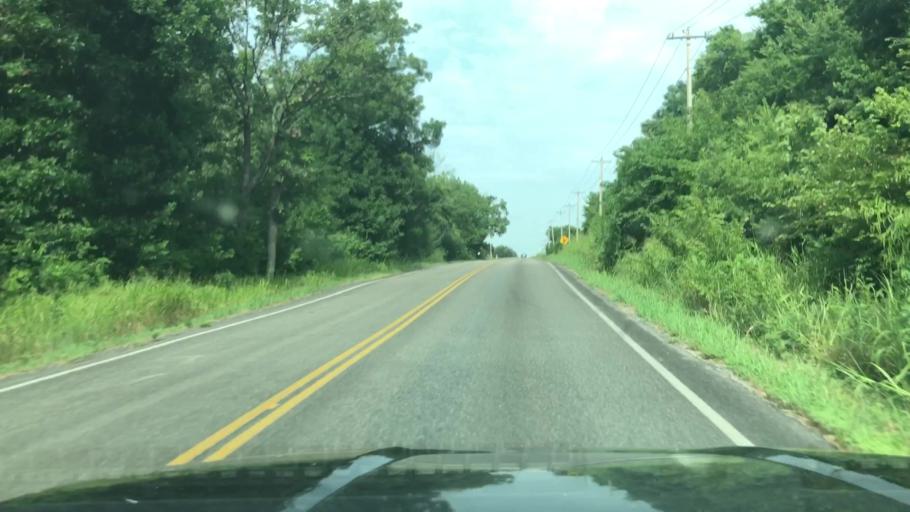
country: US
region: Oklahoma
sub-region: Tulsa County
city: Oakhurst
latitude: 36.0902
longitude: -96.1030
